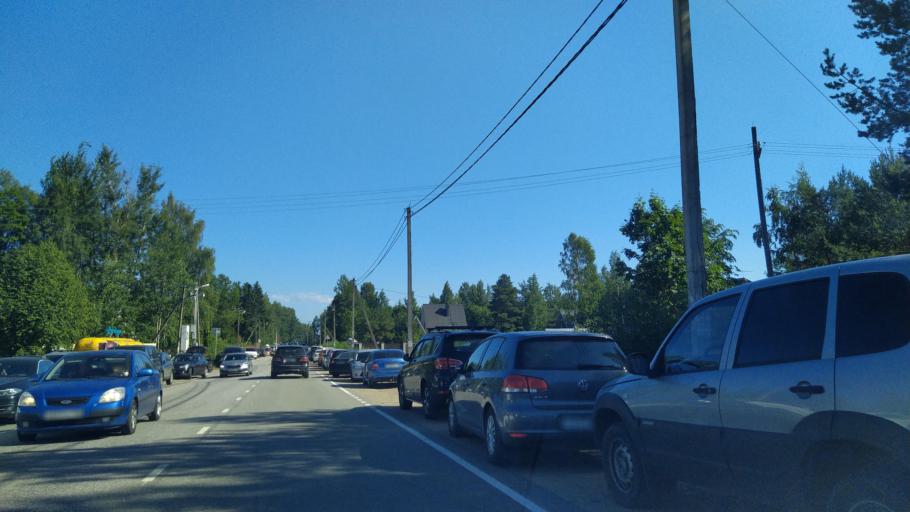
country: RU
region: Leningrad
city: Borisova Griva
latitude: 60.1175
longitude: 31.0791
